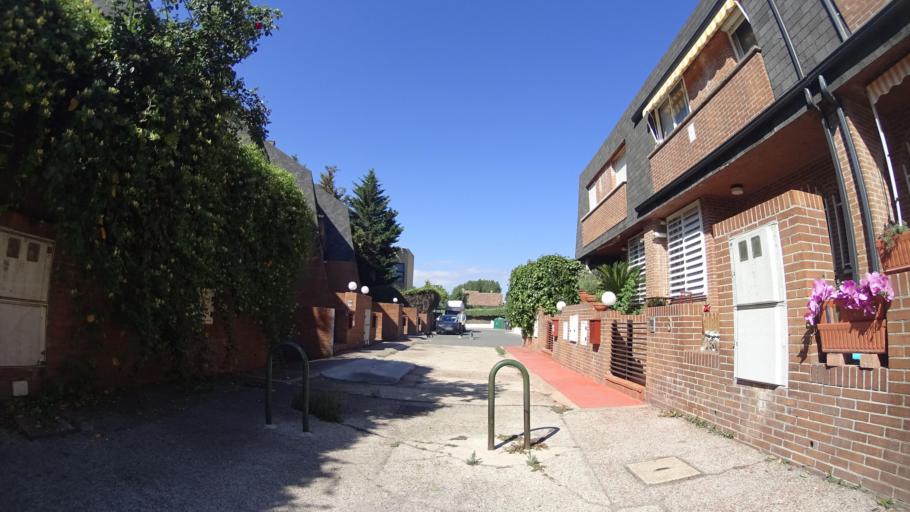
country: ES
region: Madrid
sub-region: Provincia de Madrid
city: Las Matas
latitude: 40.5480
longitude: -3.8905
